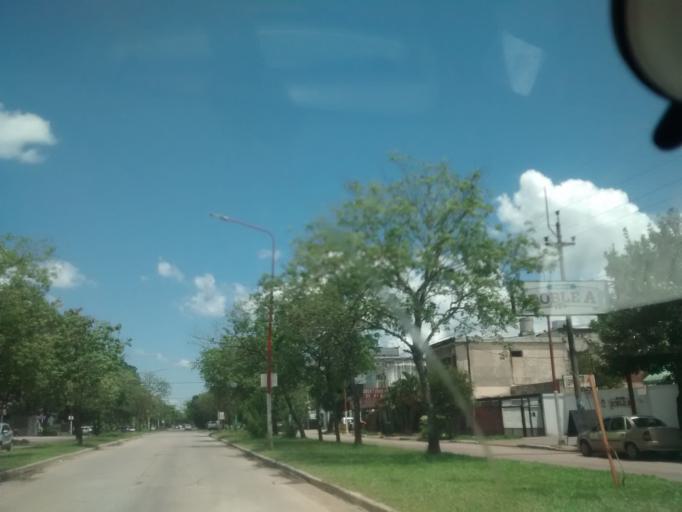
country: AR
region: Chaco
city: Resistencia
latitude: -27.4561
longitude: -58.9951
